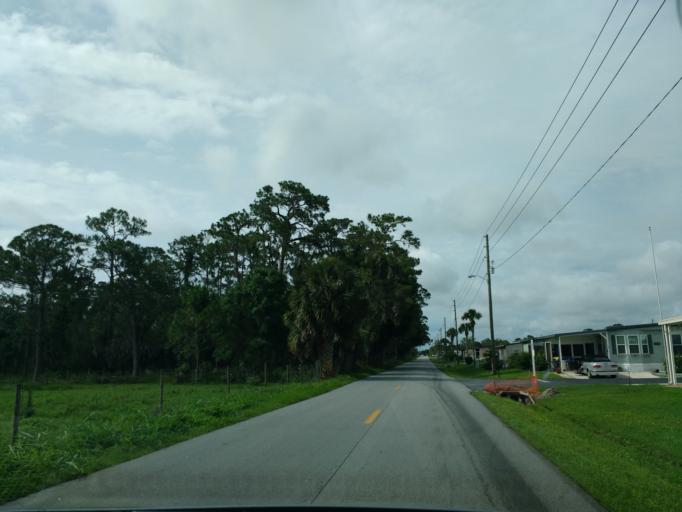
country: US
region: Florida
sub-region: Highlands County
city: Sebring
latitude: 27.4805
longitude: -81.4861
